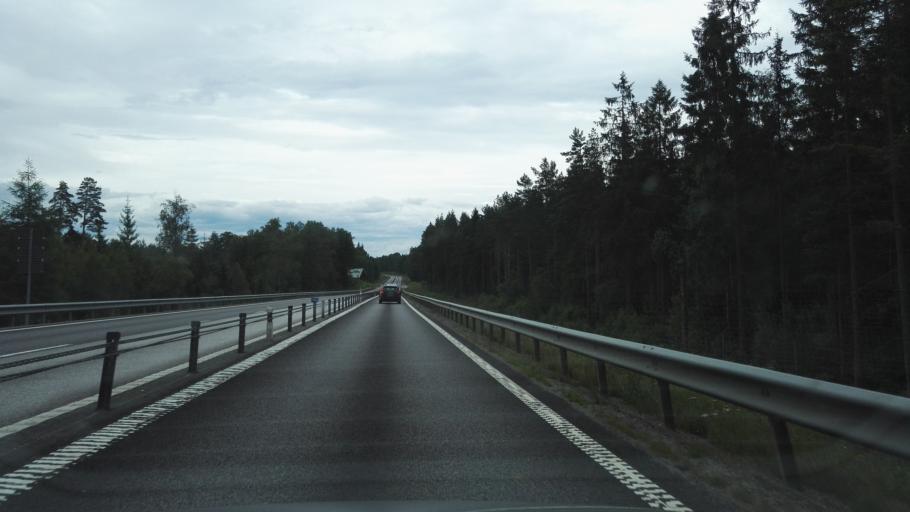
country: SE
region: Kronoberg
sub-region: Vaxjo Kommun
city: Rottne
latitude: 56.9657
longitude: 14.9620
